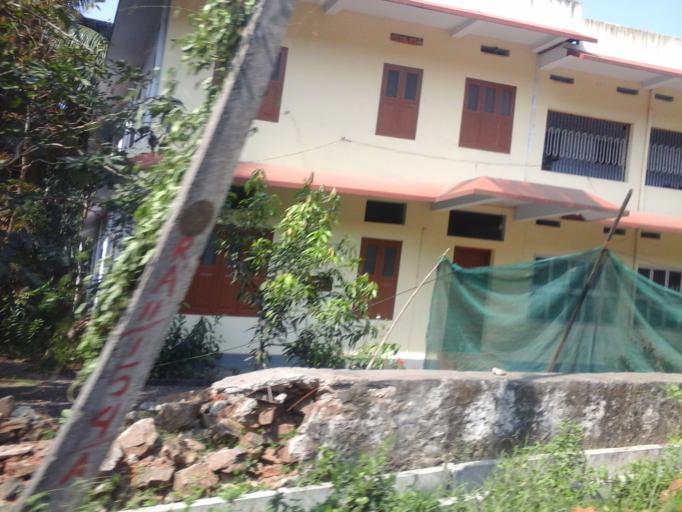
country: IN
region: Kerala
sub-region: Kottayam
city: Lalam
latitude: 9.7027
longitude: 76.6849
